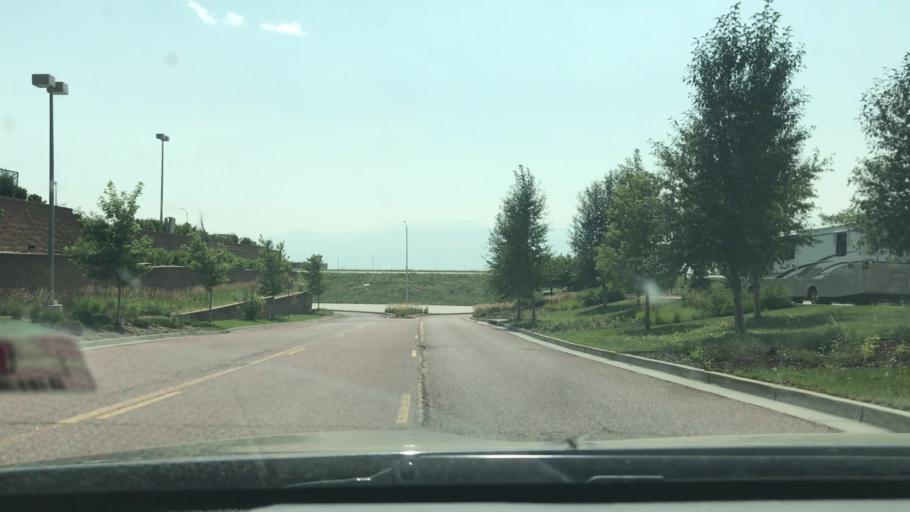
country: US
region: Colorado
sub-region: El Paso County
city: Black Forest
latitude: 38.9720
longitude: -104.7447
